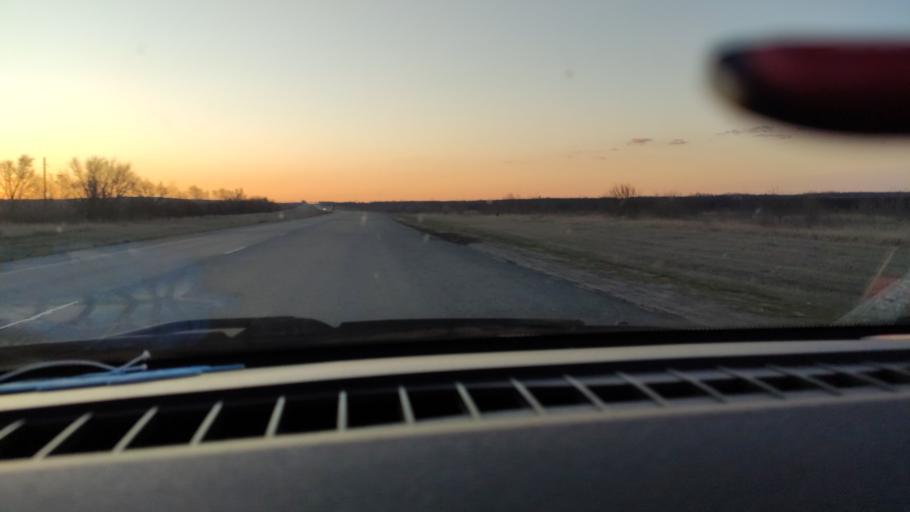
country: RU
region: Saratov
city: Yelshanka
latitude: 51.8299
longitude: 46.2423
